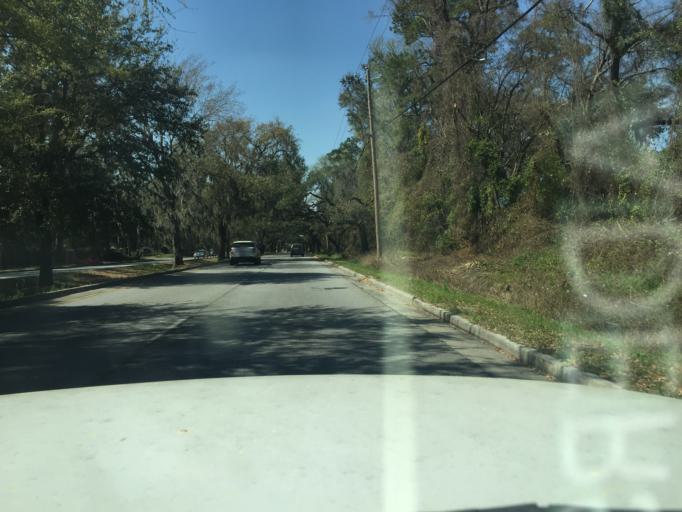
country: US
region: Georgia
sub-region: Chatham County
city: Whitemarsh Island
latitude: 32.0383
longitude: -81.0162
